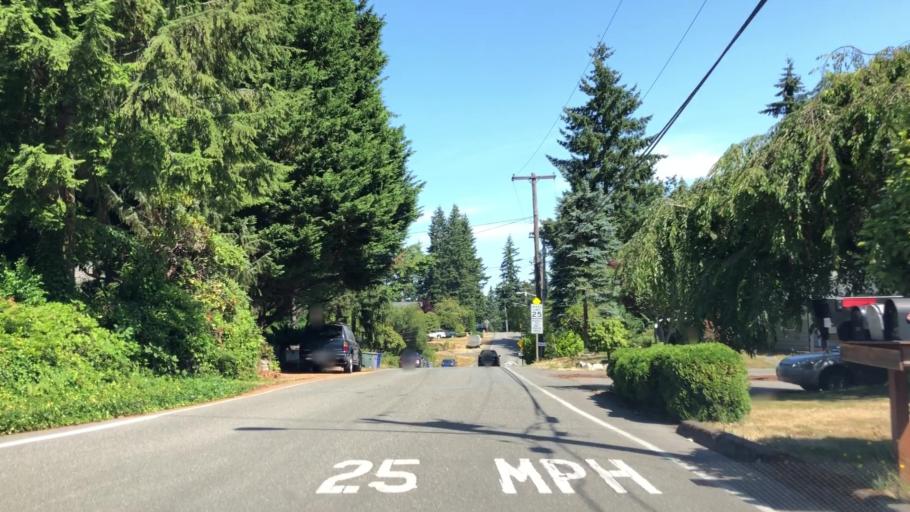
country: US
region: Washington
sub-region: King County
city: Inglewood-Finn Hill
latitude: 47.7361
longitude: -122.2411
